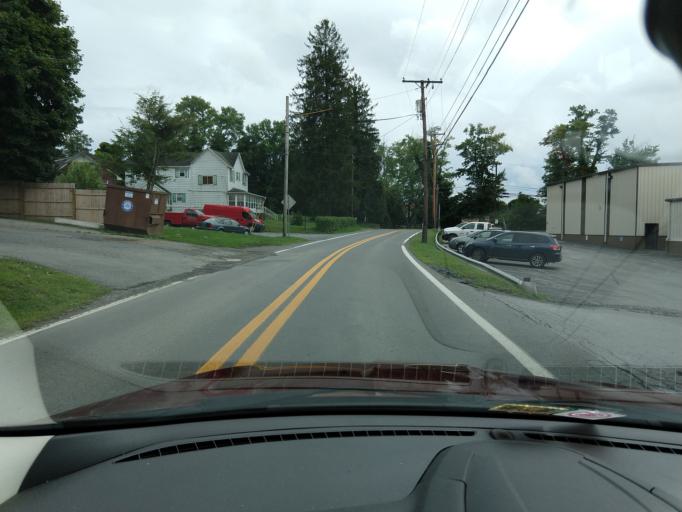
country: US
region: West Virginia
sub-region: Fayette County
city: Oak Hill
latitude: 37.9718
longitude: -81.1526
